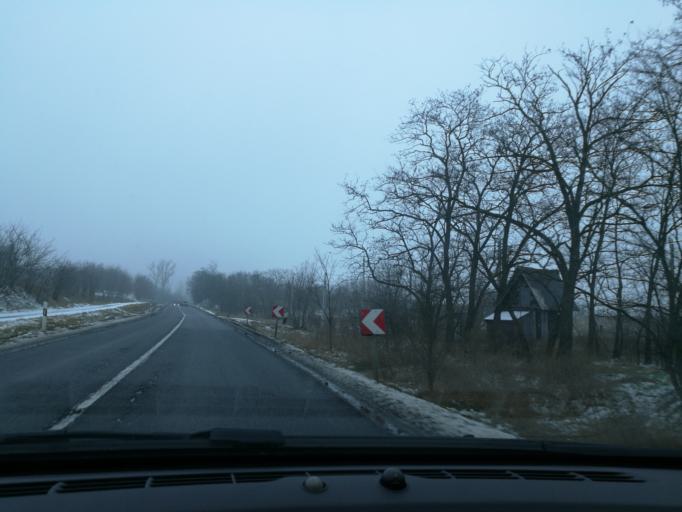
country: HU
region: Szabolcs-Szatmar-Bereg
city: Nyirpazony
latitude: 48.0015
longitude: 21.8192
